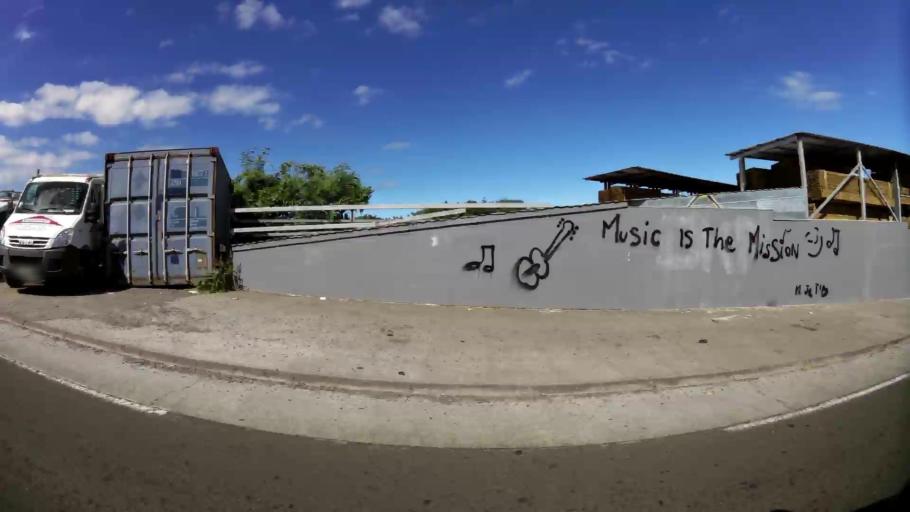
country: RE
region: Reunion
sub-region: Reunion
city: Le Tampon
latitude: -21.2950
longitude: 55.5093
